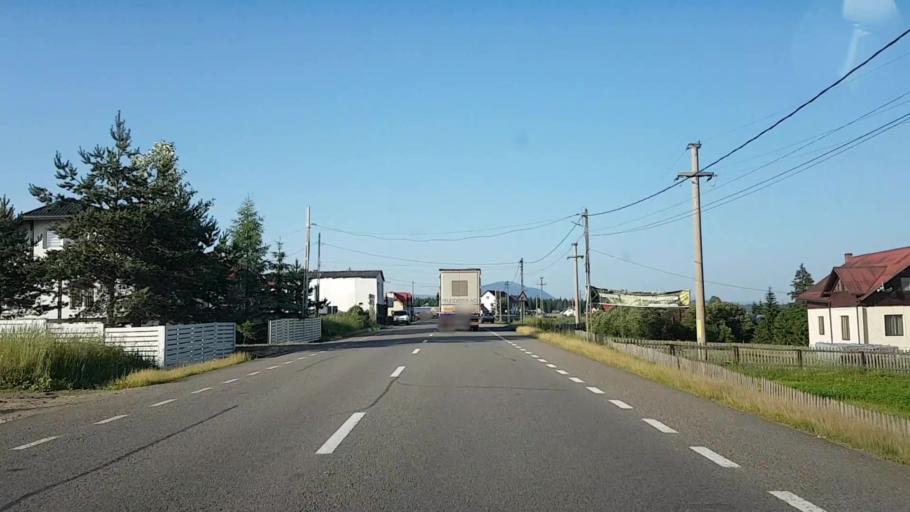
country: RO
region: Suceava
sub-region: Comuna Poiana Stampei
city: Poiana Stampei
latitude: 47.3021
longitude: 25.1097
